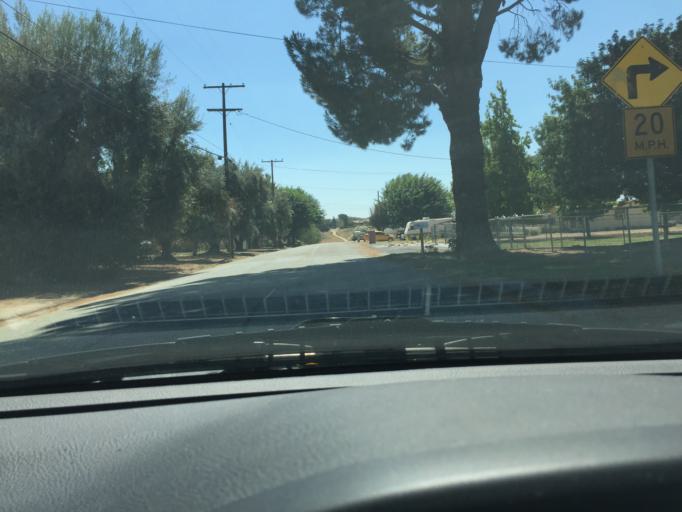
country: US
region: California
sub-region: Riverside County
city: Calimesa
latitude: 34.0014
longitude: -117.0258
